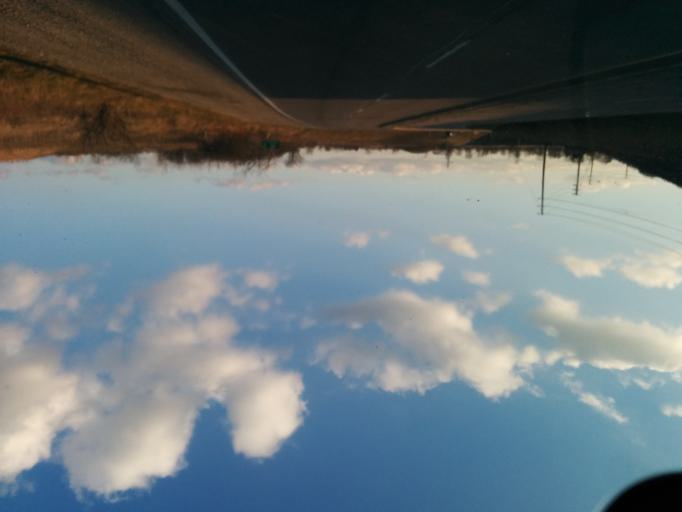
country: CA
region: Ontario
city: Oakville
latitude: 43.4937
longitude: -79.6667
